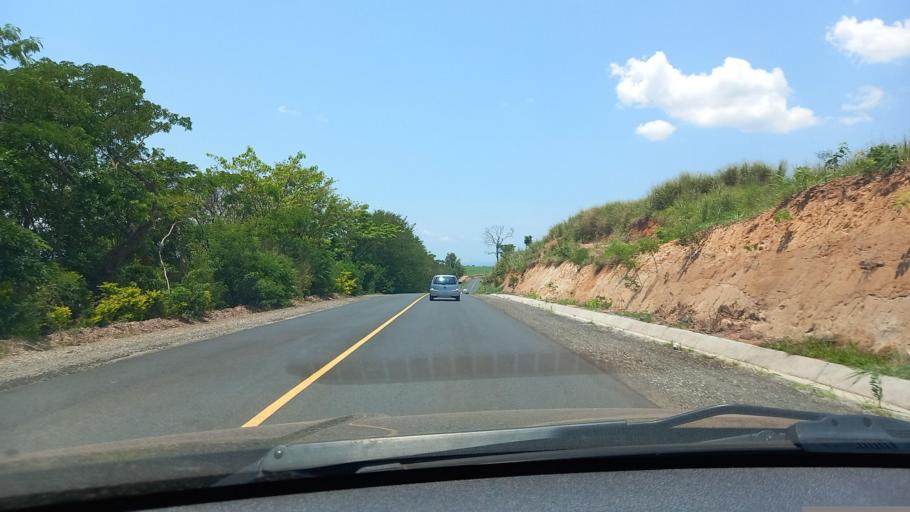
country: BR
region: Sao Paulo
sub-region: Moji-Guacu
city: Mogi-Gaucu
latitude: -22.3528
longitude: -46.8722
